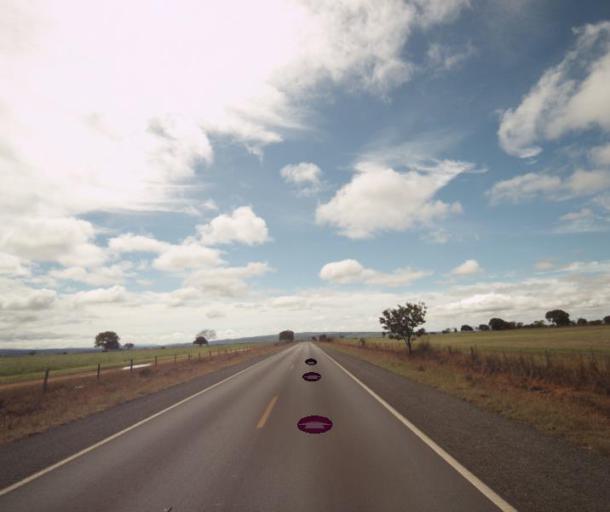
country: BR
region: Goias
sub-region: Padre Bernardo
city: Padre Bernardo
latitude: -15.2173
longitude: -48.6126
